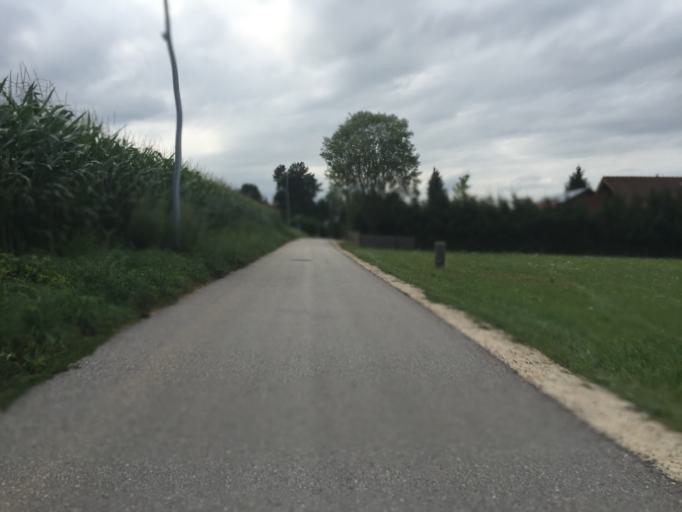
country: AT
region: Carinthia
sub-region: Politischer Bezirk Volkermarkt
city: Feistritz ob Bleiburg
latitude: 46.5564
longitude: 14.7807
